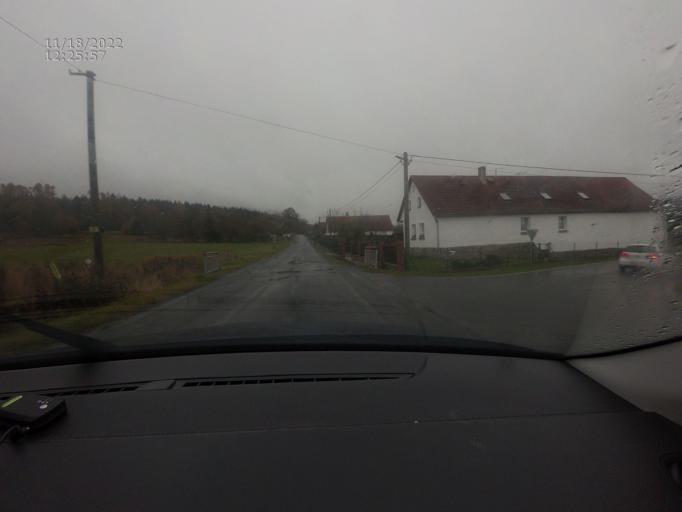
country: CZ
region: Plzensky
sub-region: Okres Klatovy
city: Planice
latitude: 49.4375
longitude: 13.5119
